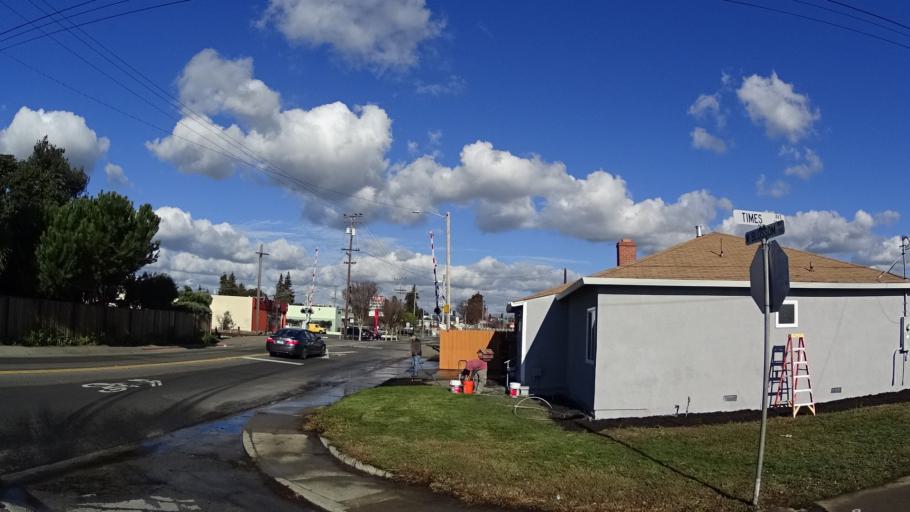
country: US
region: California
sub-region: Alameda County
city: Cherryland
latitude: 37.6754
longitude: -122.1110
